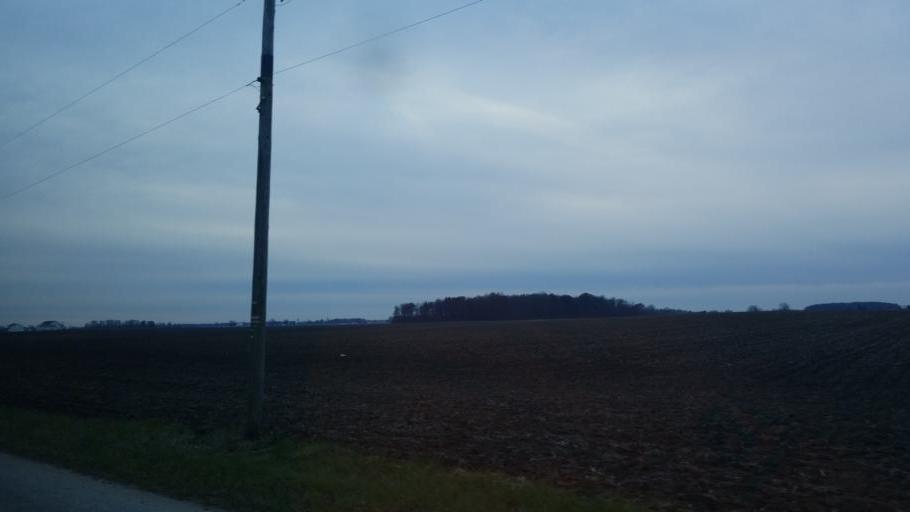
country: US
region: Indiana
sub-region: Adams County
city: Decatur
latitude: 40.7894
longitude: -84.8801
